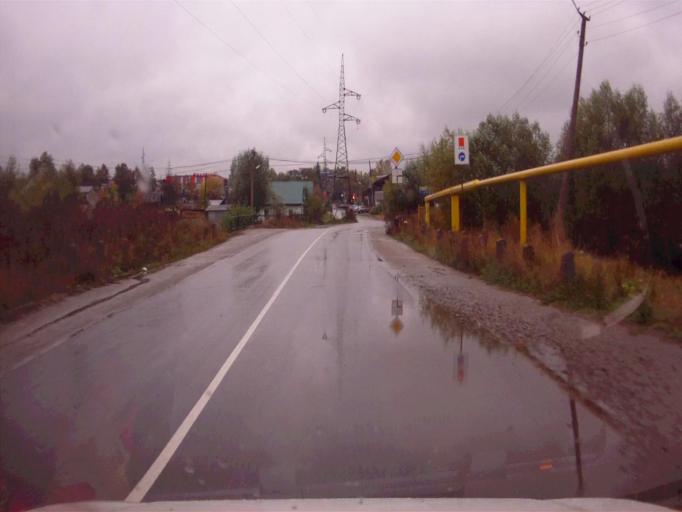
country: RU
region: Chelyabinsk
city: Kyshtym
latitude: 55.7153
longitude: 60.5444
